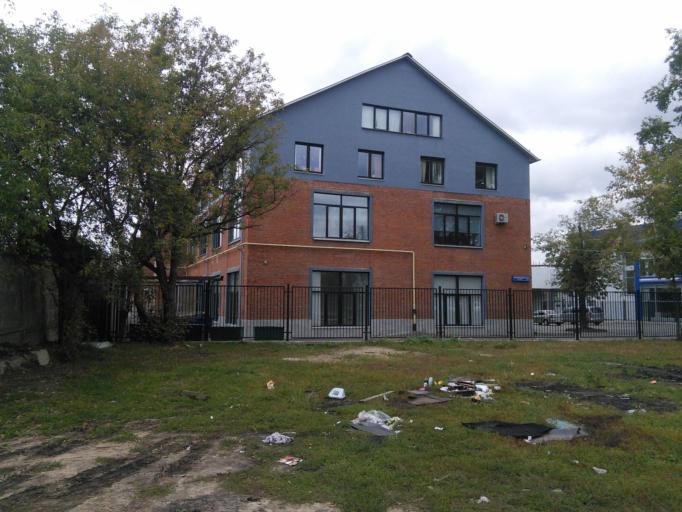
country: RU
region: Moskovskaya
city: Kozhukhovo
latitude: 55.7025
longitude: 37.6547
